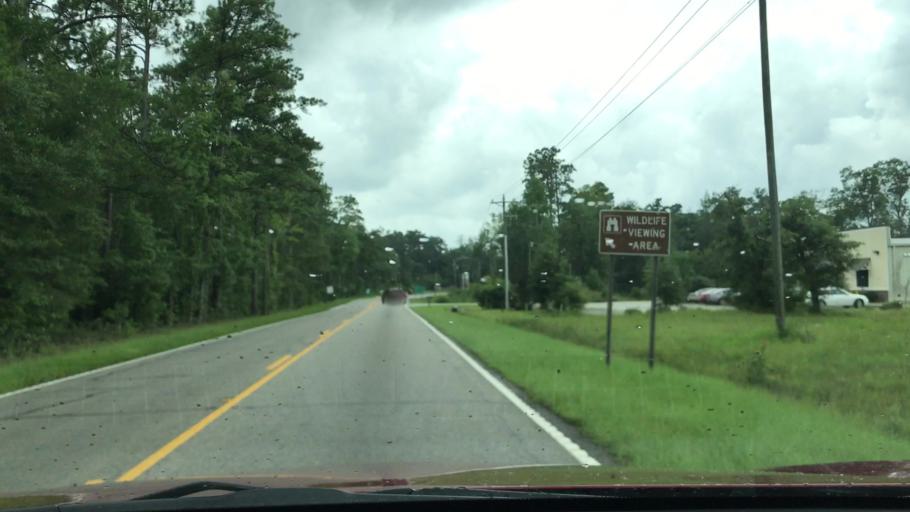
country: US
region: South Carolina
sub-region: Georgetown County
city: Georgetown
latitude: 33.4849
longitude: -79.2678
